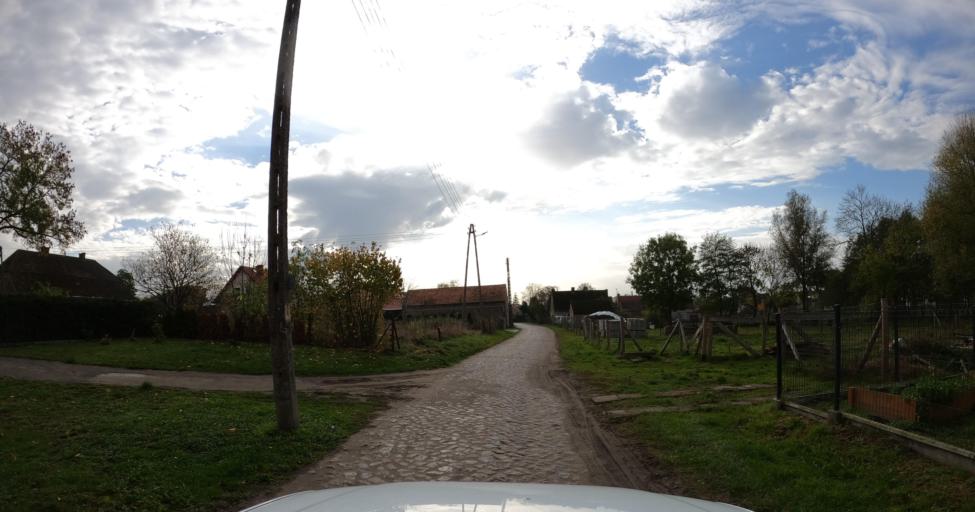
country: PL
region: West Pomeranian Voivodeship
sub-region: Powiat kamienski
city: Kamien Pomorski
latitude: 53.9756
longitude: 14.8480
